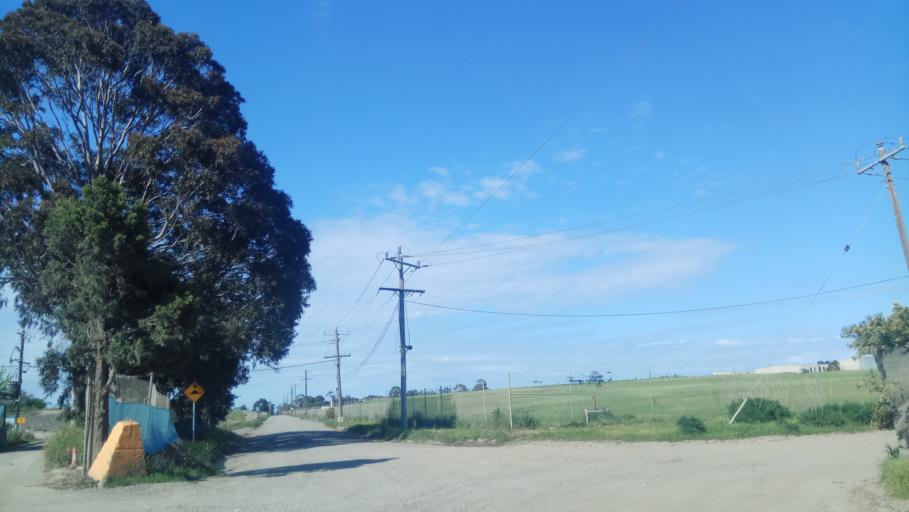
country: AU
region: Victoria
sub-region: Kingston
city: Clayton South
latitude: -37.9465
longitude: 145.1204
